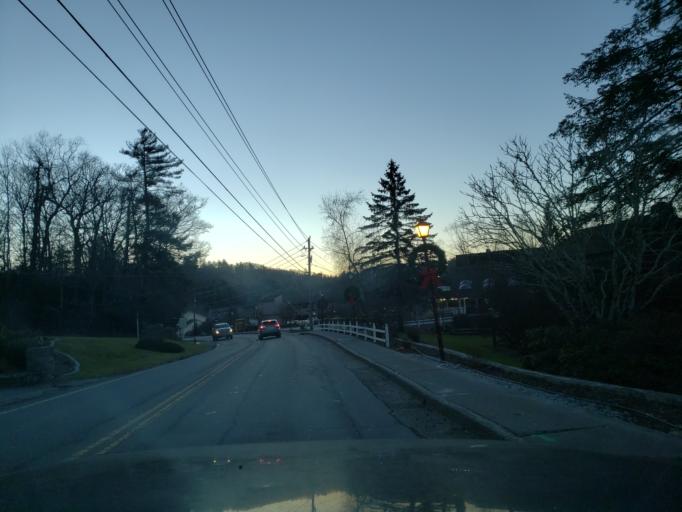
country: US
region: North Carolina
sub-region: Watauga County
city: Blowing Rock
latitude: 36.1349
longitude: -81.6759
